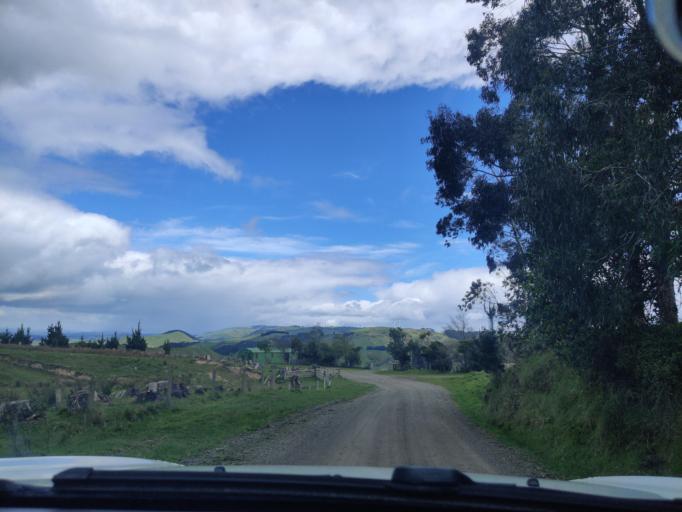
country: NZ
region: Manawatu-Wanganui
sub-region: Palmerston North City
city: Palmerston North
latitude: -40.2861
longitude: 175.8611
